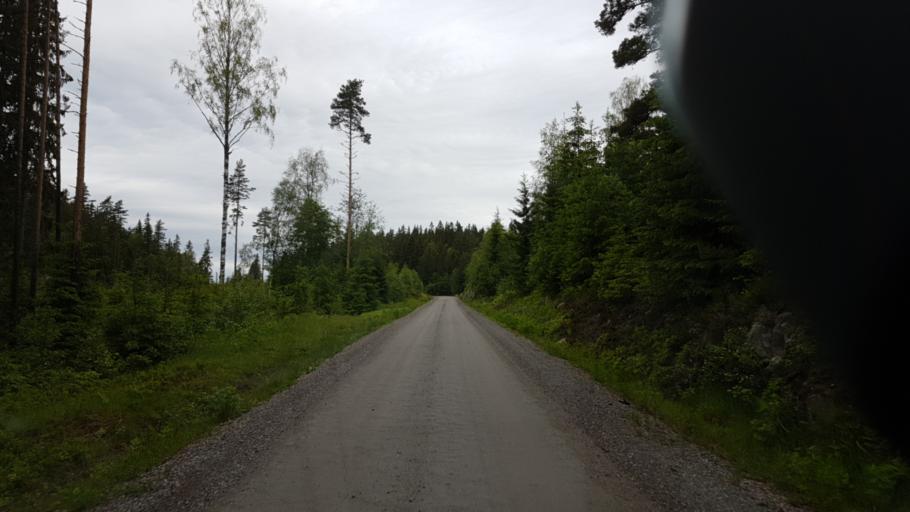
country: NO
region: Ostfold
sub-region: Romskog
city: Romskog
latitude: 59.7062
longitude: 12.0469
